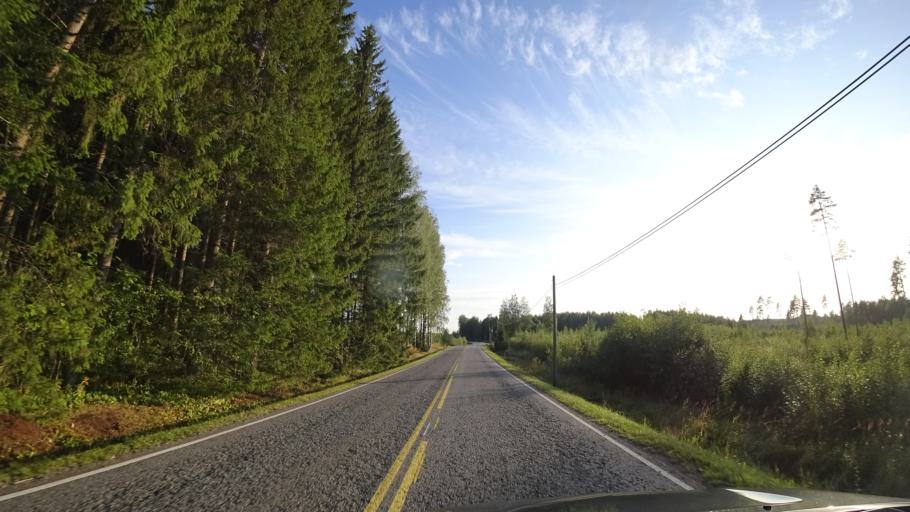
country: FI
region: Haeme
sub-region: Haemeenlinna
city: Lammi
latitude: 61.0486
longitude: 24.9478
